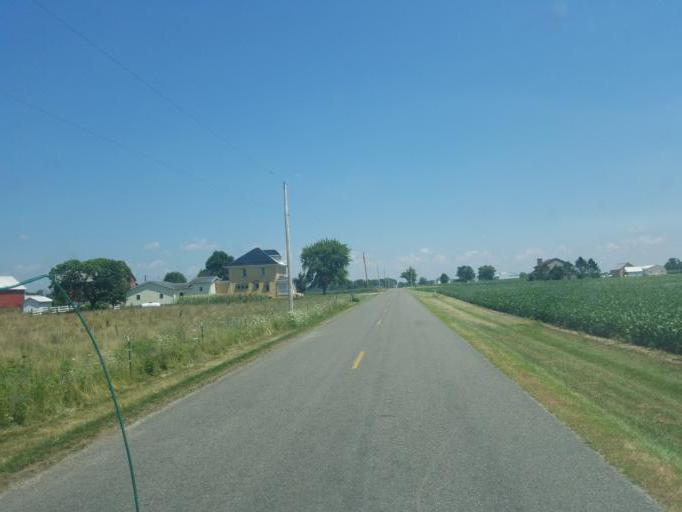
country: US
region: Ohio
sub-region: Shelby County
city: Botkins
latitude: 40.4823
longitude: -84.2096
